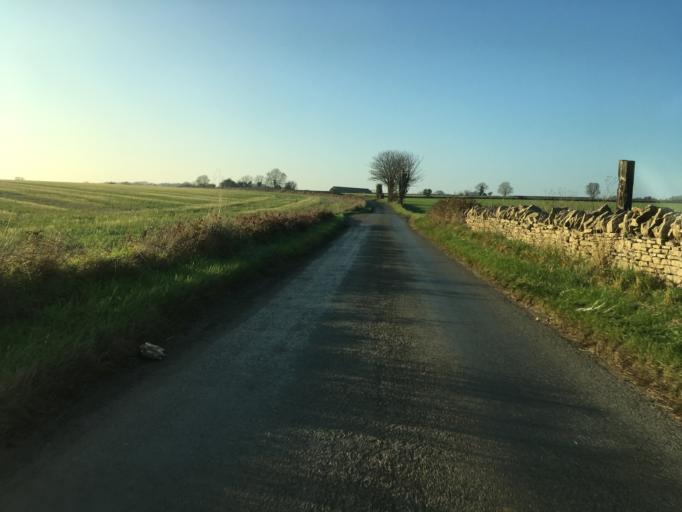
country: GB
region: England
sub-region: South Gloucestershire
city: Horton
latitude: 51.5554
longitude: -2.3258
